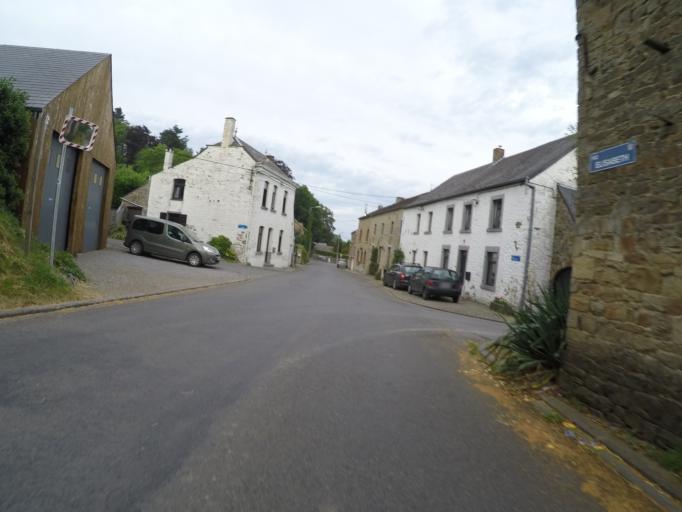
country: BE
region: Wallonia
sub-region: Province de Namur
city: Assesse
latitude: 50.3372
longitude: 4.9829
